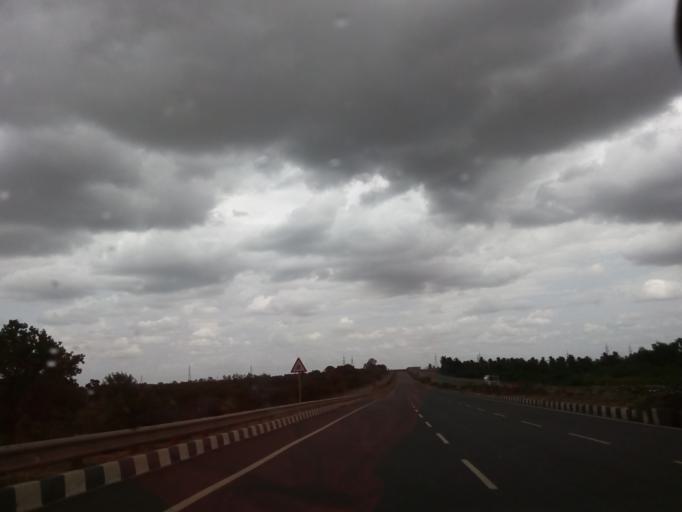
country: IN
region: Karnataka
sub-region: Chitradurga
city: Hiriyur
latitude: 14.0028
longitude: 76.5881
